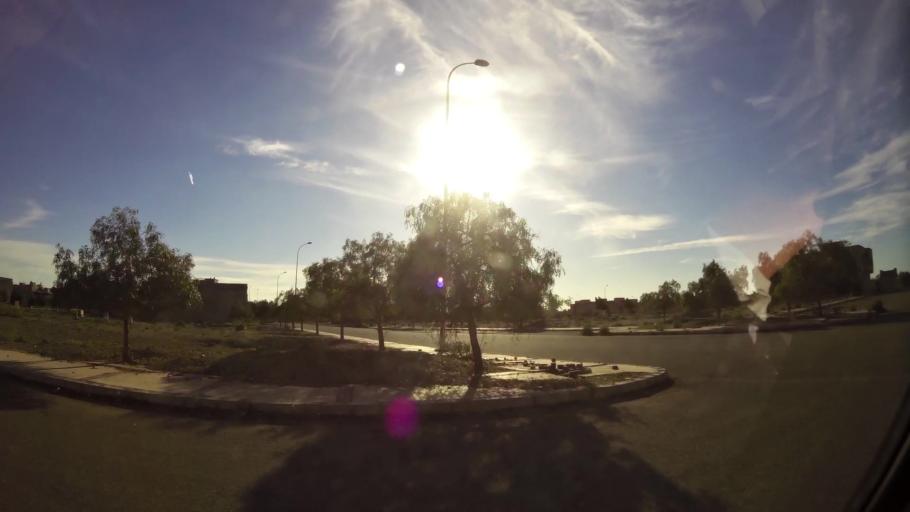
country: MA
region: Marrakech-Tensift-Al Haouz
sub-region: Marrakech
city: Marrakesh
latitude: 31.7582
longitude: -8.0948
